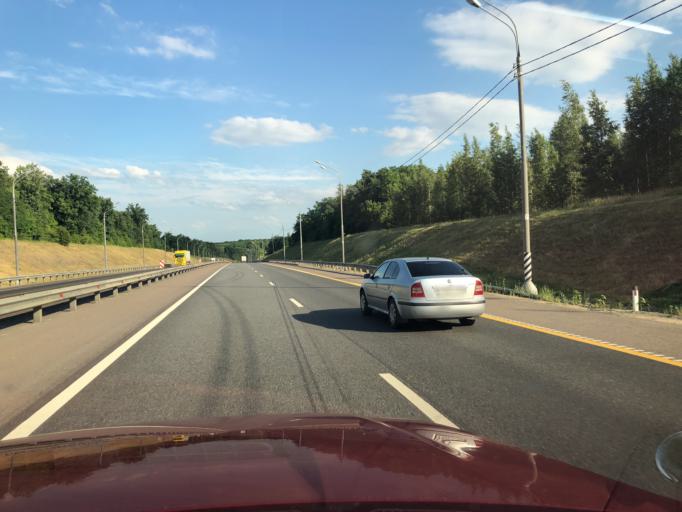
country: RU
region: Lipetsk
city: Zadonsk
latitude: 52.4123
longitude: 38.8469
